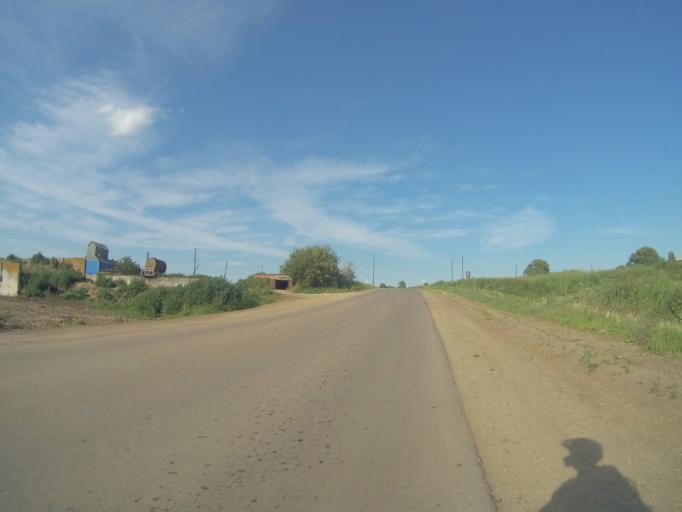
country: RU
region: Vladimir
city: Stavrovo
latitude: 56.2876
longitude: 40.1830
